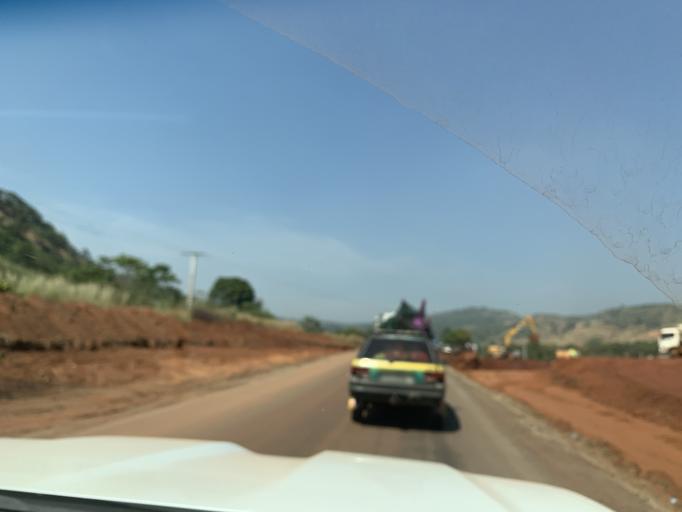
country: GN
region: Mamou
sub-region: Mamou Prefecture
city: Mamou
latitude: 10.2033
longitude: -12.4668
